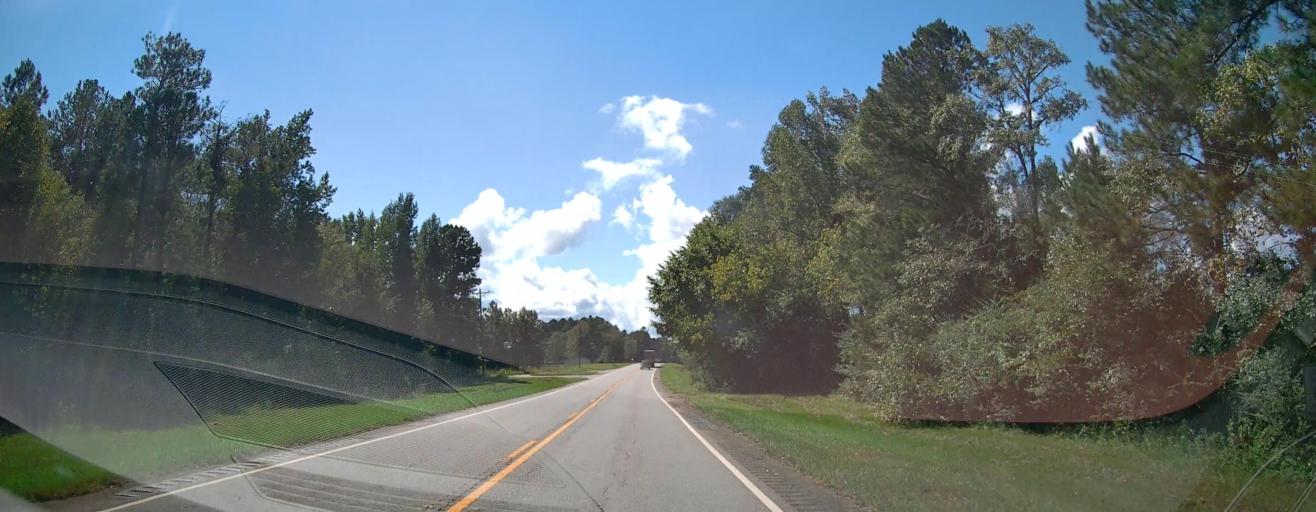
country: US
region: Georgia
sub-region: Jones County
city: Gray
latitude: 33.0426
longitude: -83.3953
